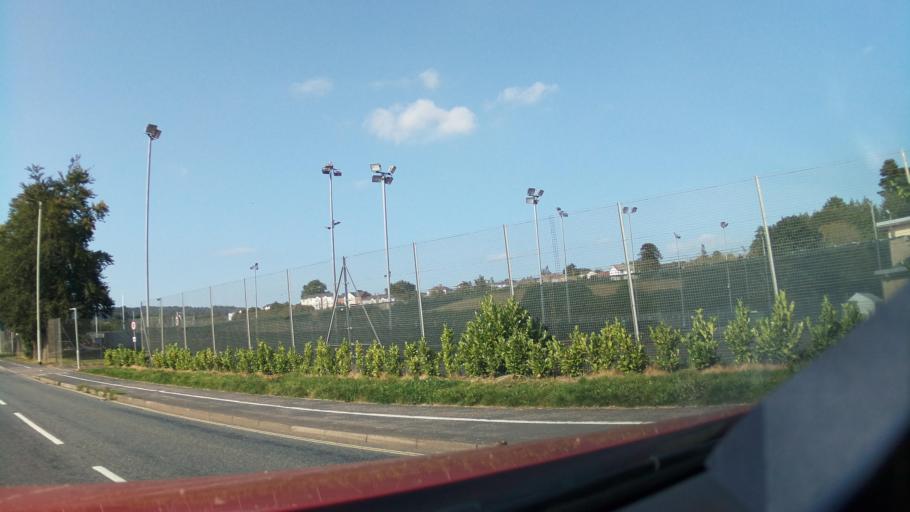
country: GB
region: England
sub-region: Devon
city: Tiverton
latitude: 50.9102
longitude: -3.4893
